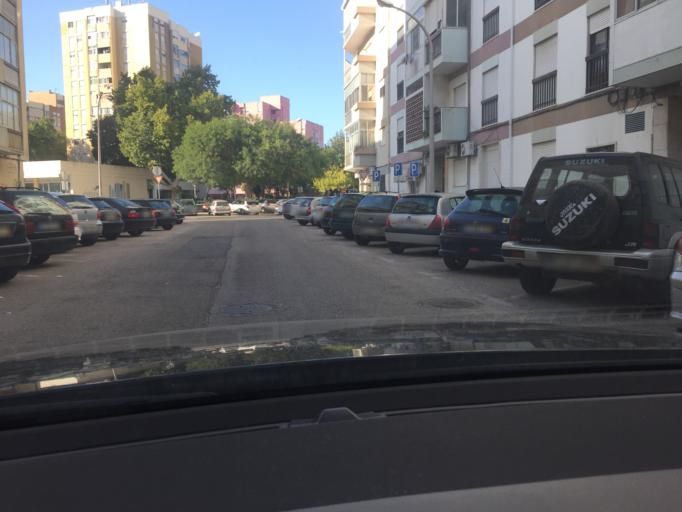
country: PT
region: Setubal
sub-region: Setubal
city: Setubal
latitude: 38.5310
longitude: -8.8874
